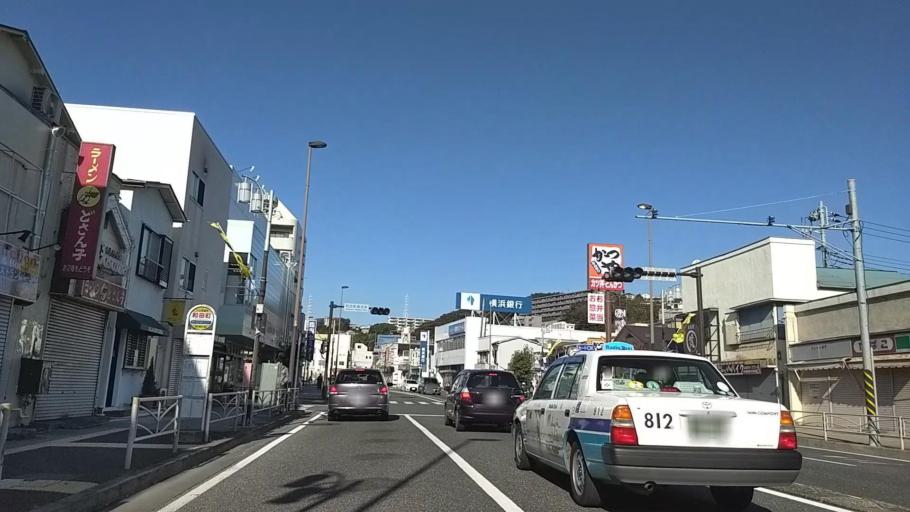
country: JP
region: Kanagawa
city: Yokohama
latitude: 35.4648
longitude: 139.5896
